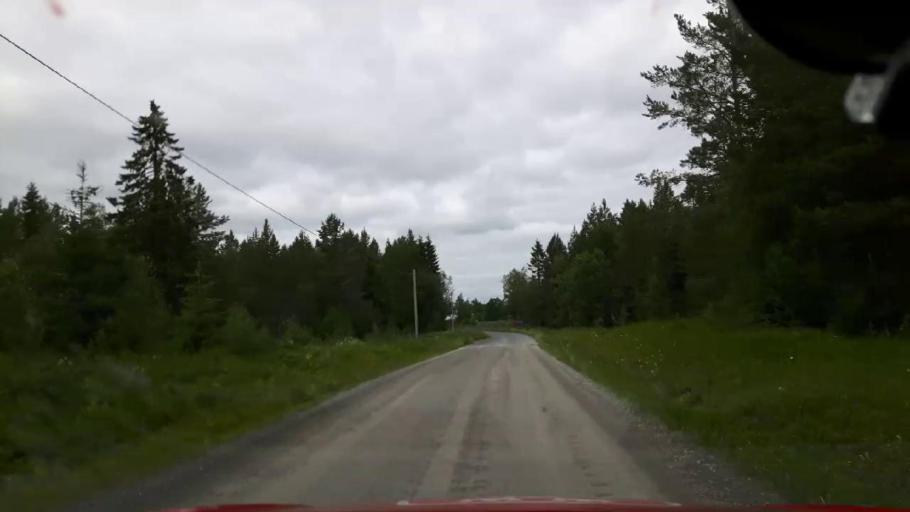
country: SE
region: Jaemtland
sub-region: OEstersunds Kommun
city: Brunflo
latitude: 63.0681
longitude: 14.8945
